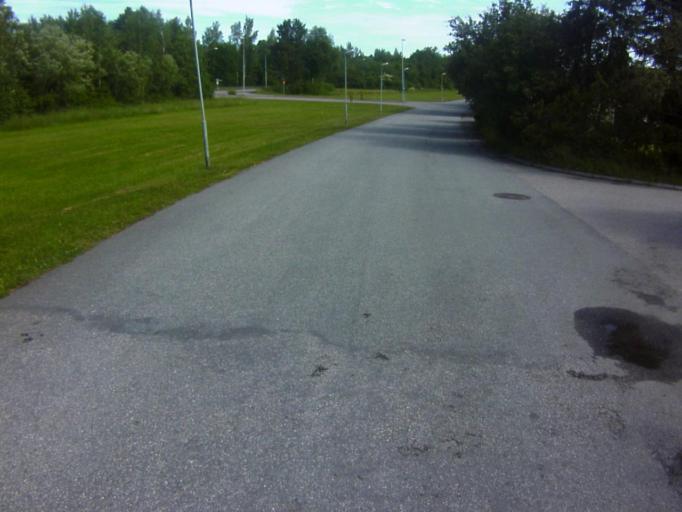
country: SE
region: Soedermanland
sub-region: Eskilstuna Kommun
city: Skogstorp
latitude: 59.3477
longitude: 16.4423
